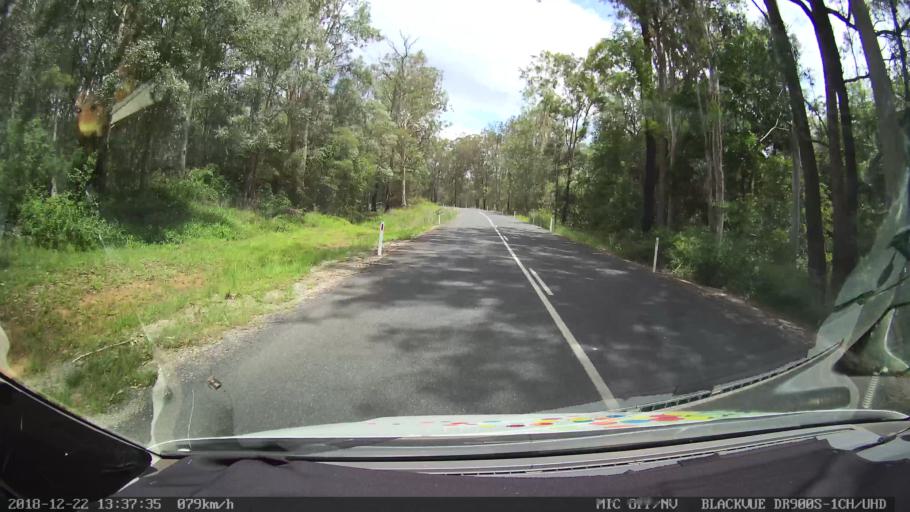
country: AU
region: New South Wales
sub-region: Clarence Valley
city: Coutts Crossing
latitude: -29.8915
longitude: 152.7881
